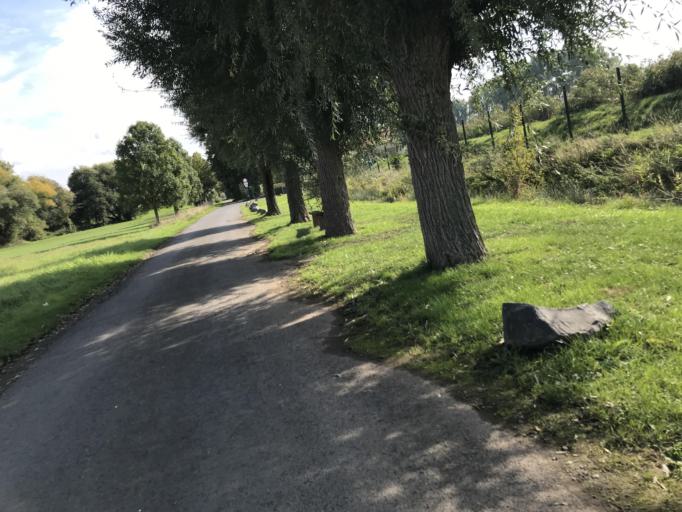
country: DE
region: Hesse
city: Gudensberg
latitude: 51.1571
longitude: 9.3683
